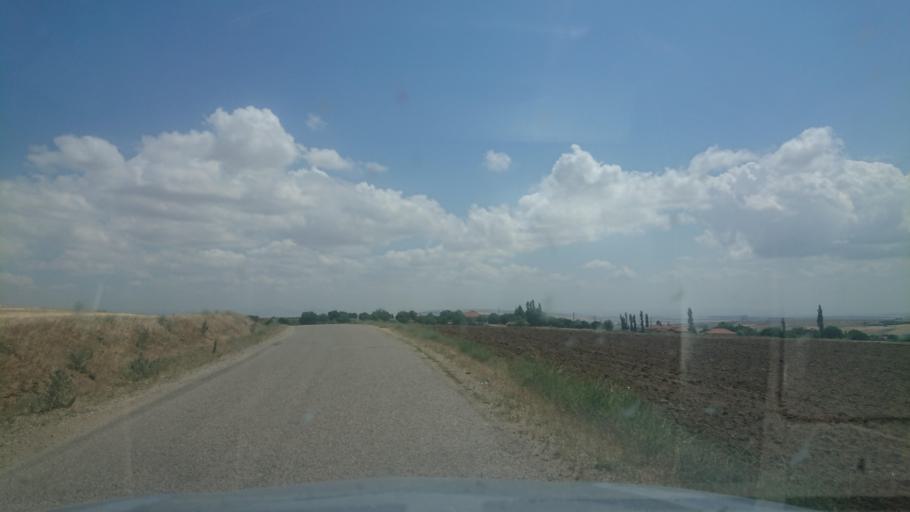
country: TR
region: Aksaray
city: Agacoren
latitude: 38.8697
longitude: 33.9386
